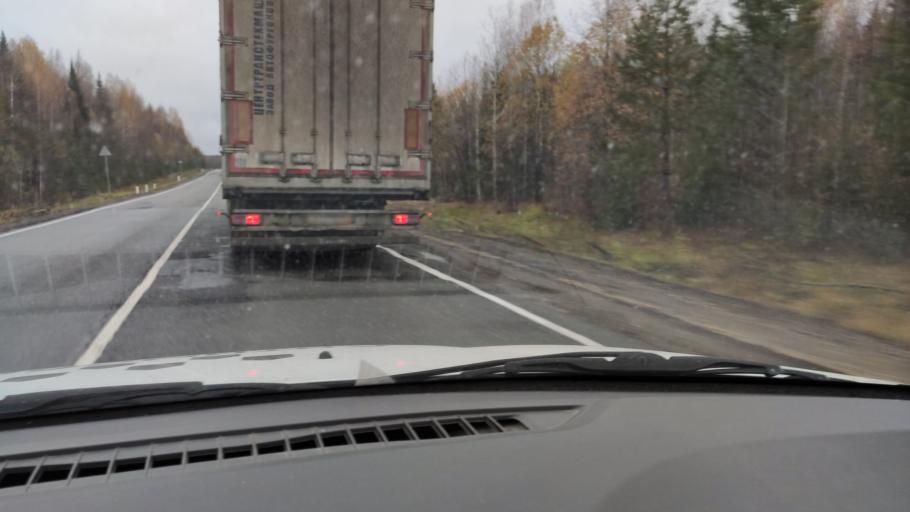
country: RU
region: Kirov
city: Omutninsk
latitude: 58.7515
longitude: 52.0541
